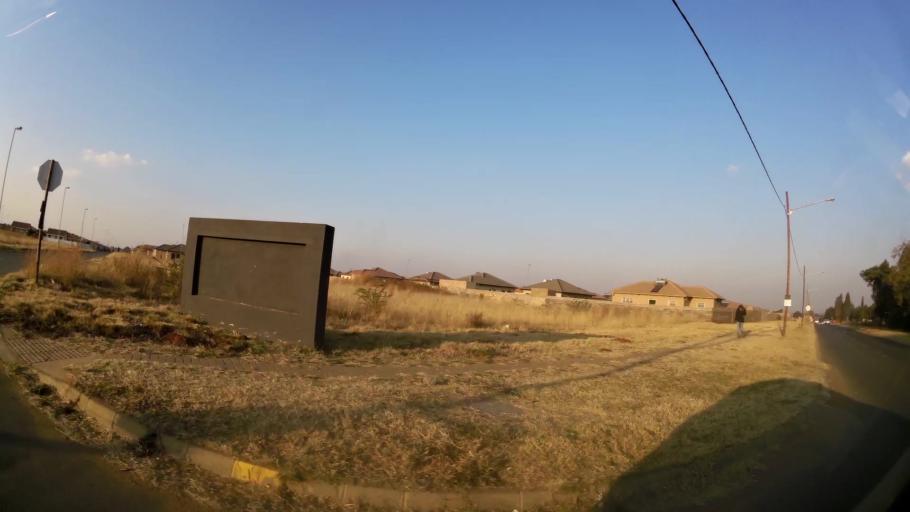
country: ZA
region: Gauteng
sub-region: Ekurhuleni Metropolitan Municipality
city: Benoni
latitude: -26.1416
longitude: 28.3790
